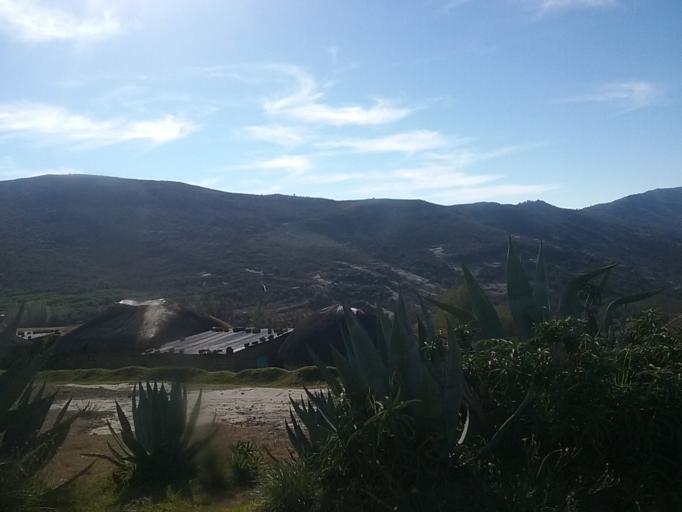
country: LS
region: Berea
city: Teyateyaneng
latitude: -29.2379
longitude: 27.8811
